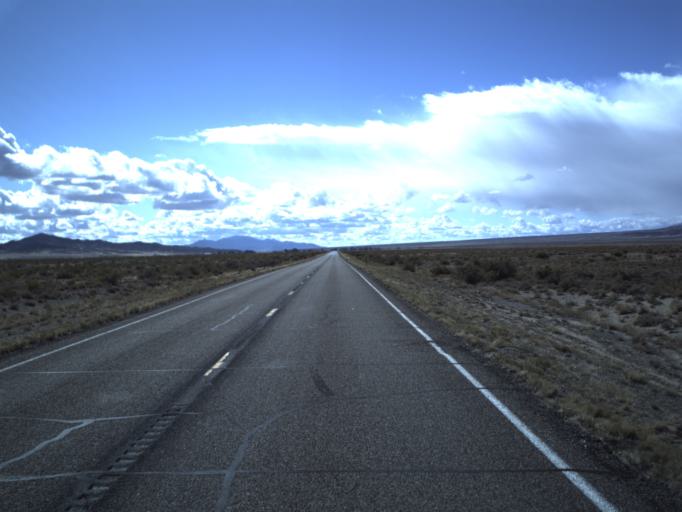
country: US
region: Nevada
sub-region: White Pine County
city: McGill
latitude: 39.0049
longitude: -114.0350
